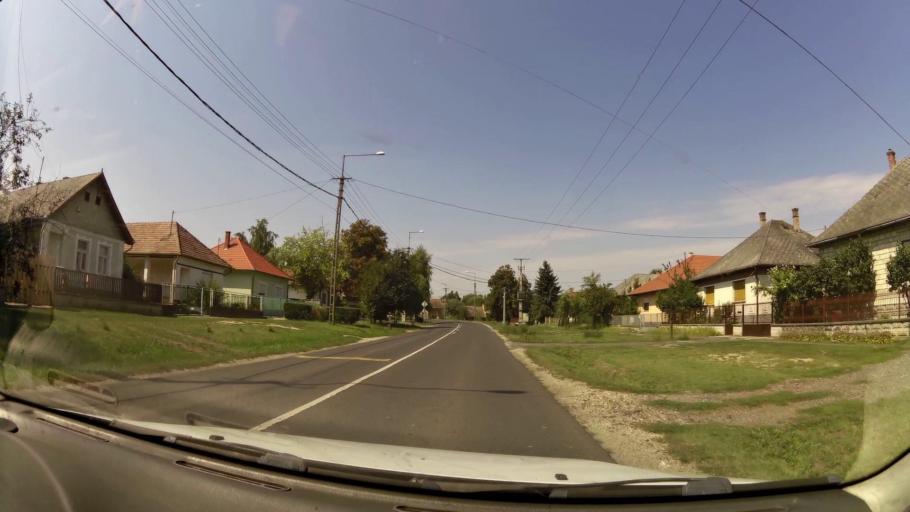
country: HU
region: Pest
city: Suelysap
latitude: 47.4467
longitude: 19.5439
